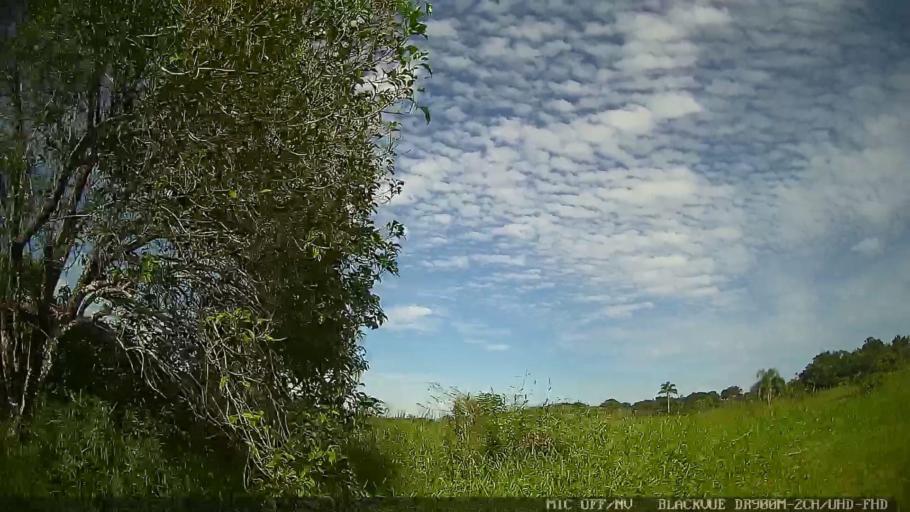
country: BR
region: Sao Paulo
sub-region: Iguape
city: Iguape
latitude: -24.7645
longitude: -47.5877
